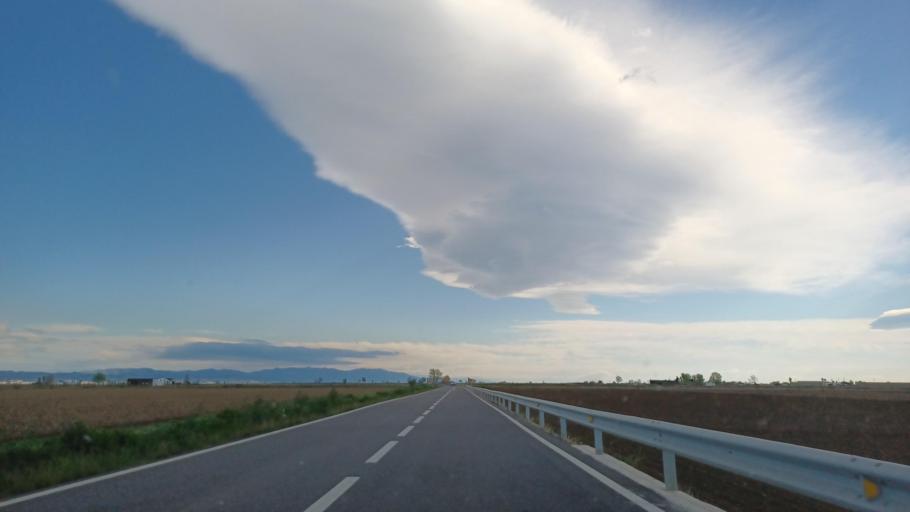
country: ES
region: Catalonia
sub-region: Provincia de Tarragona
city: Deltebre
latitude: 40.7346
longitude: 0.7121
